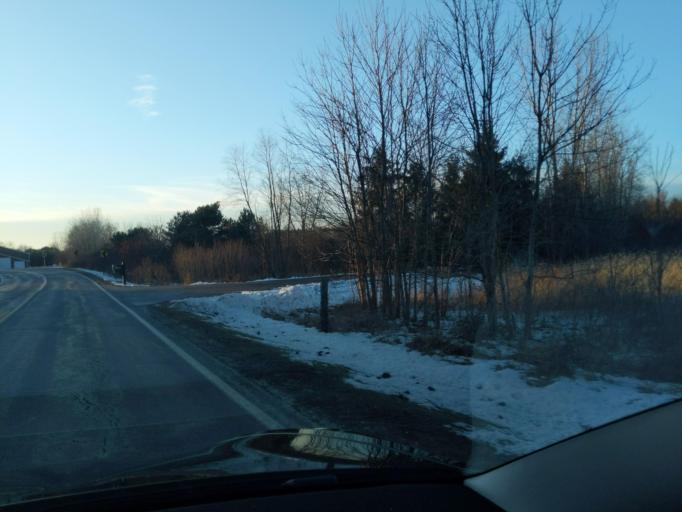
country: US
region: Michigan
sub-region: Ingham County
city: Mason
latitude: 42.5343
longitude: -84.3070
